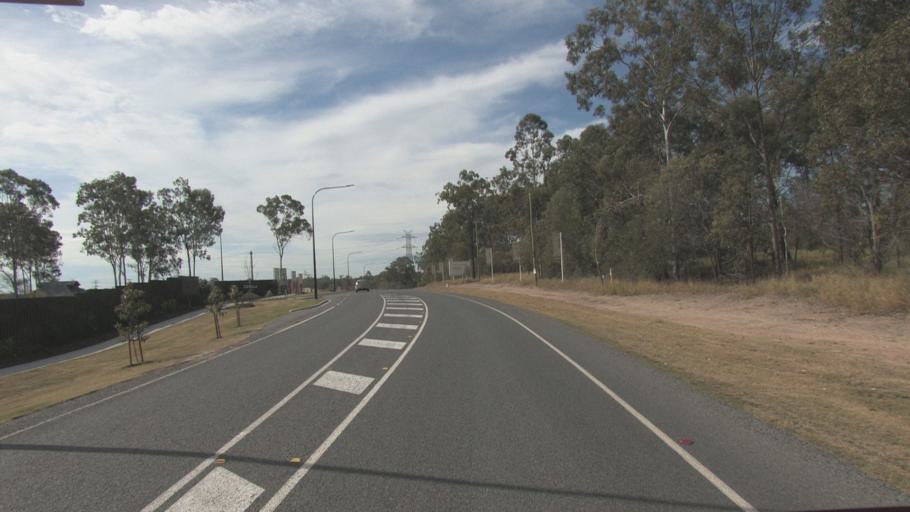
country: AU
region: Queensland
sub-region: Logan
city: North Maclean
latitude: -27.7370
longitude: 152.9740
